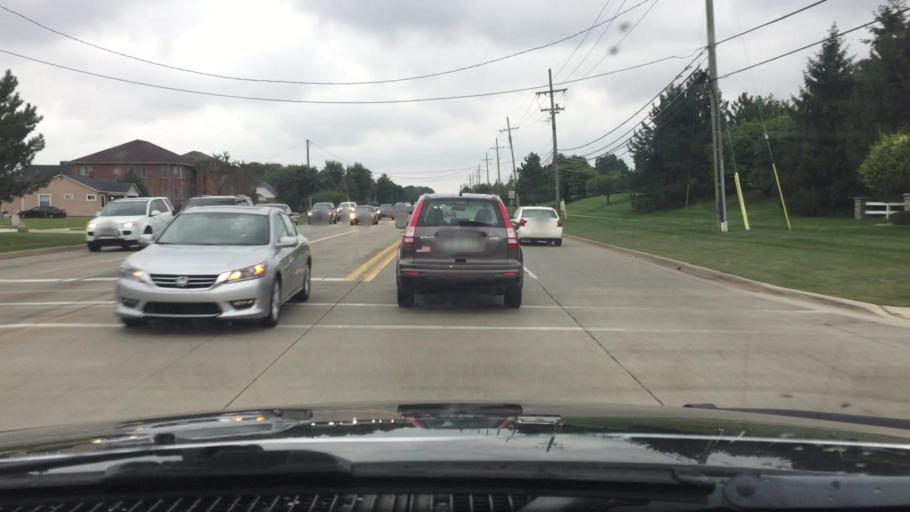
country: US
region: Michigan
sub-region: Macomb County
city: Utica
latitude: 42.6081
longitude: -83.0714
